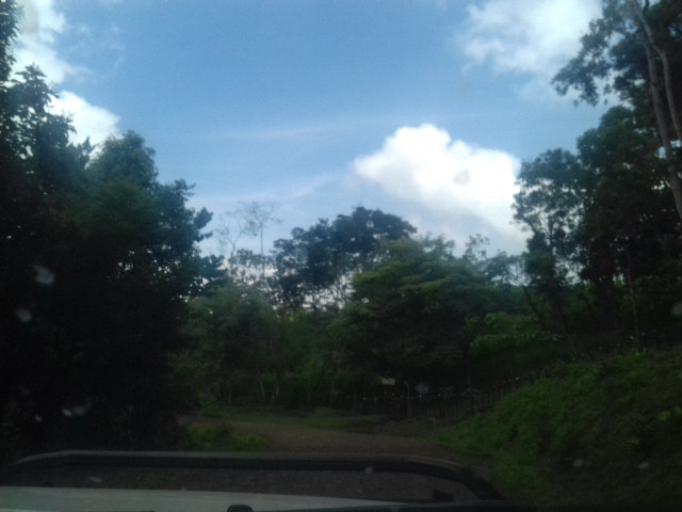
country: NI
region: Matagalpa
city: Matiguas
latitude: 12.9201
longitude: -85.3647
